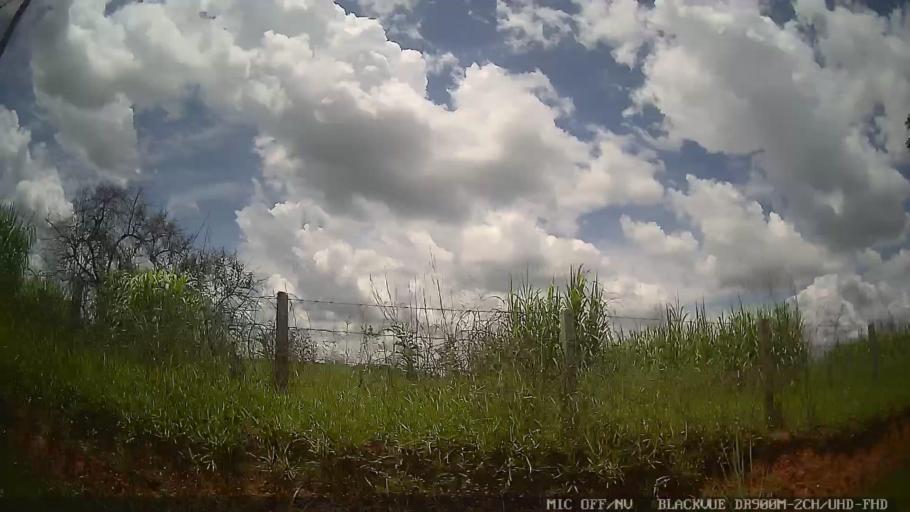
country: BR
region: Sao Paulo
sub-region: Atibaia
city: Atibaia
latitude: -23.1005
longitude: -46.6297
